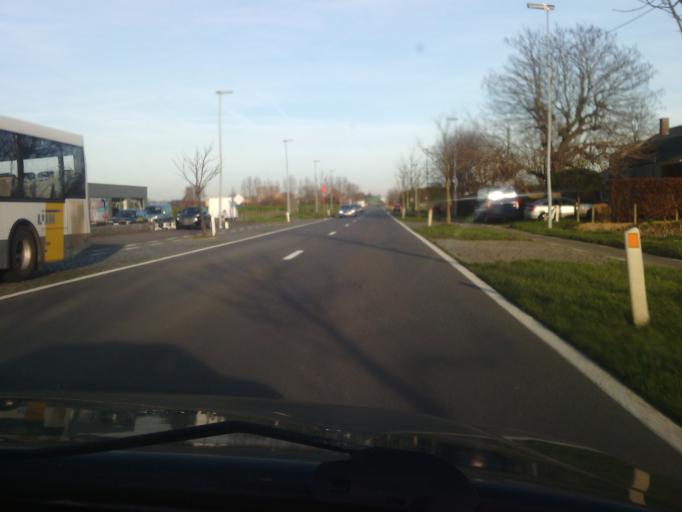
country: BE
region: Flanders
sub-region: Provincie Oost-Vlaanderen
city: Berlare
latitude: 51.0164
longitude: 4.0388
